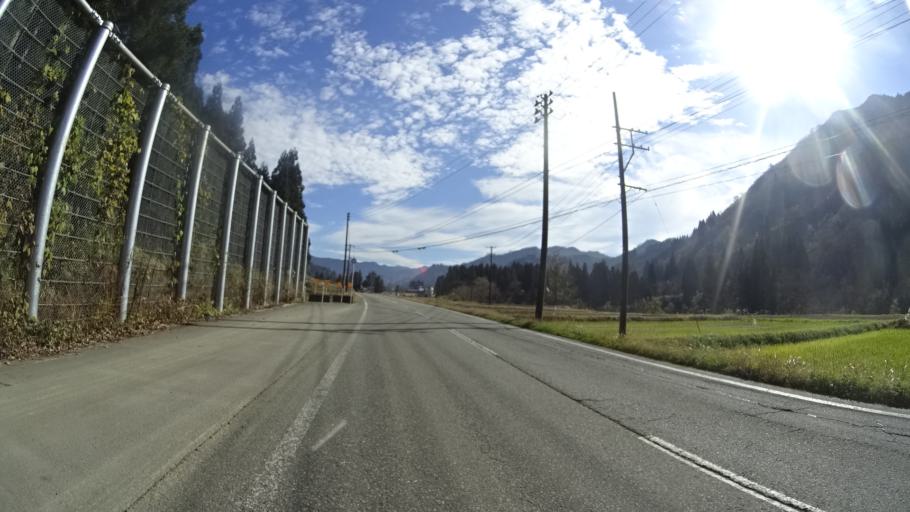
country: JP
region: Niigata
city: Muikamachi
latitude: 37.2208
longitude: 139.0296
